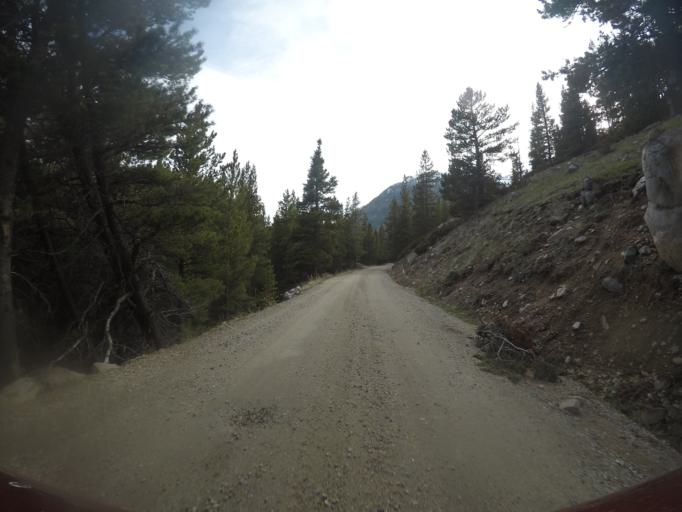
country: US
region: Montana
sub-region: Carbon County
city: Red Lodge
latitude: 45.0252
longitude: -109.4448
